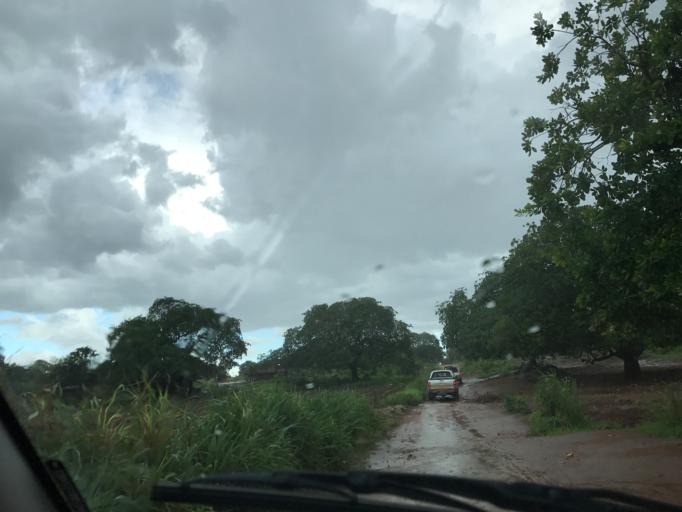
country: MZ
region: Nampula
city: Nacala
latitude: -14.7531
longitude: 39.9931
